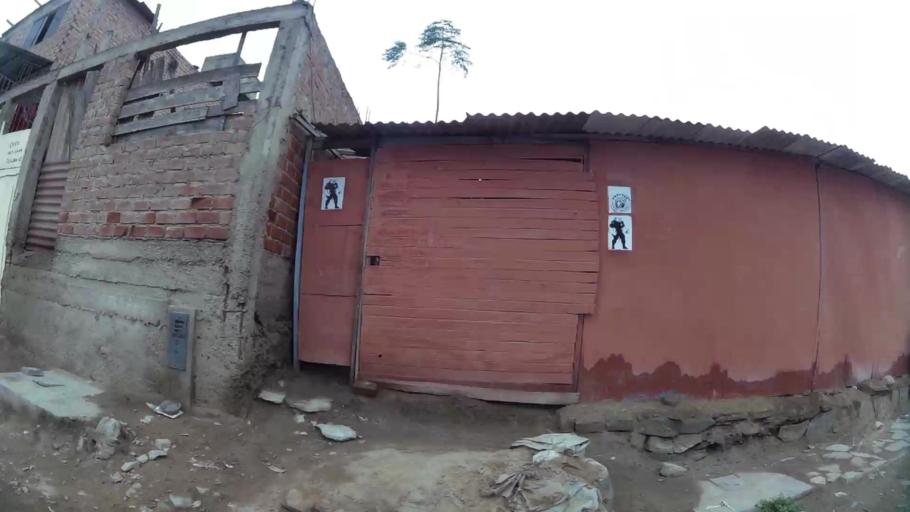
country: PE
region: Lima
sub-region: Lima
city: Surco
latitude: -12.2221
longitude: -76.9179
